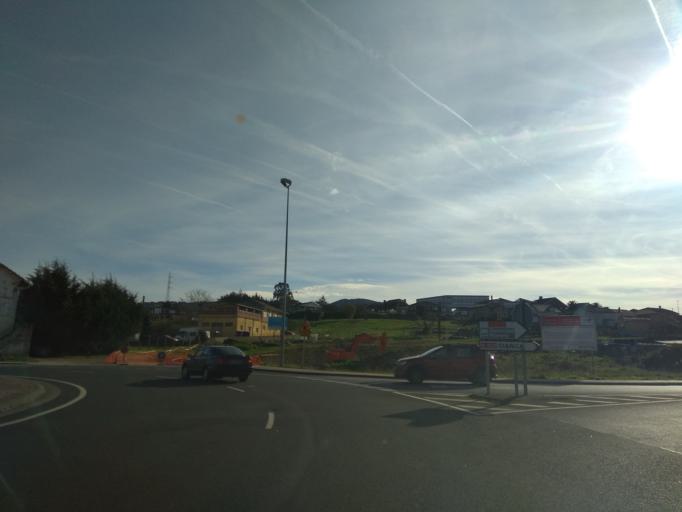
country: ES
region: Cantabria
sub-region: Provincia de Cantabria
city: El Astillero
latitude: 43.4051
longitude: -3.8376
